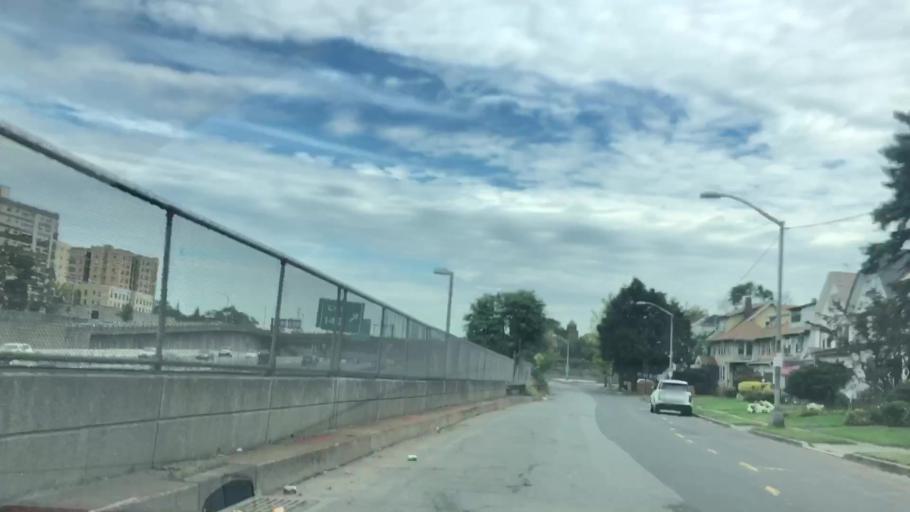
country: US
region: New Jersey
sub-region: Essex County
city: East Orange
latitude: 40.7539
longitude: -74.2103
